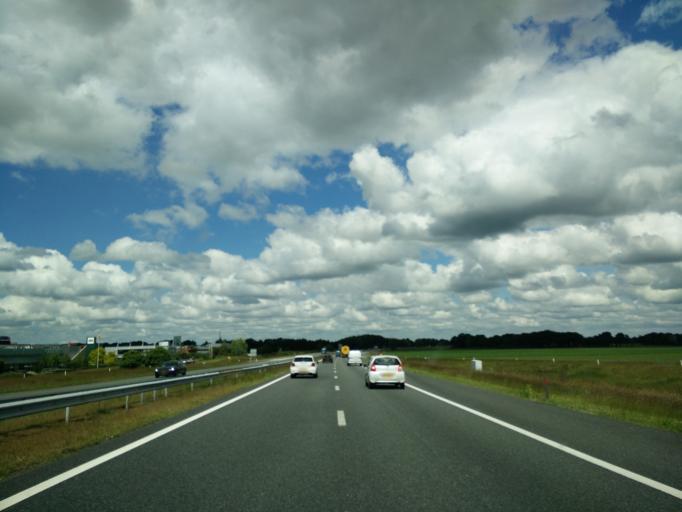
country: NL
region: Drenthe
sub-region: Gemeente Tynaarlo
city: Tynaarlo
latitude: 53.0820
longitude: 6.6039
